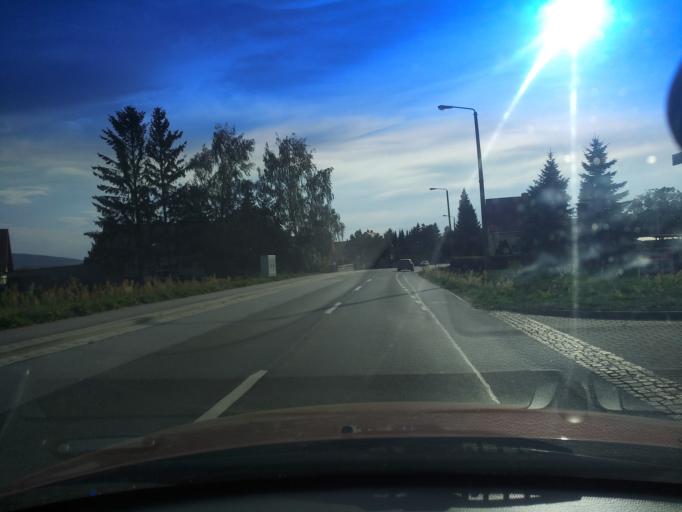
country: DE
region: Saxony
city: Bautzen
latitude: 51.1989
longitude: 14.4651
